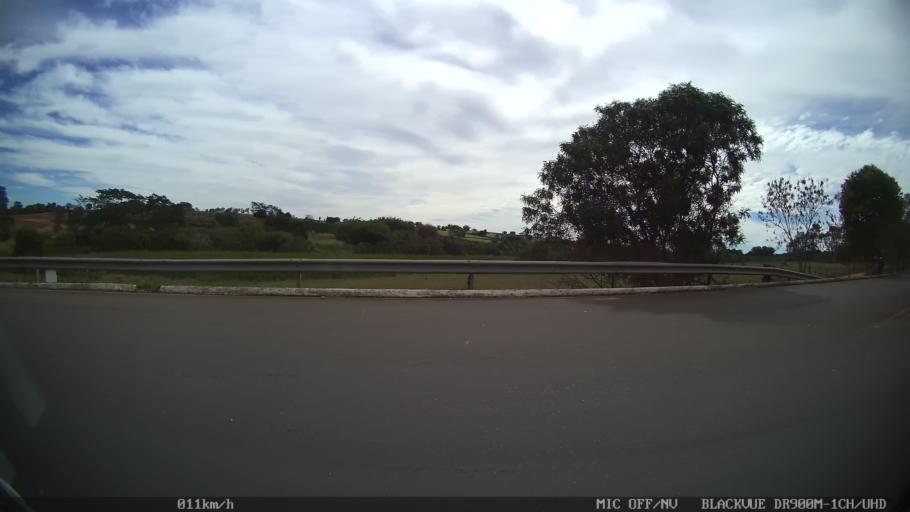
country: BR
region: Sao Paulo
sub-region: Santa Adelia
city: Santa Adelia
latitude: -21.3689
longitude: -48.7475
